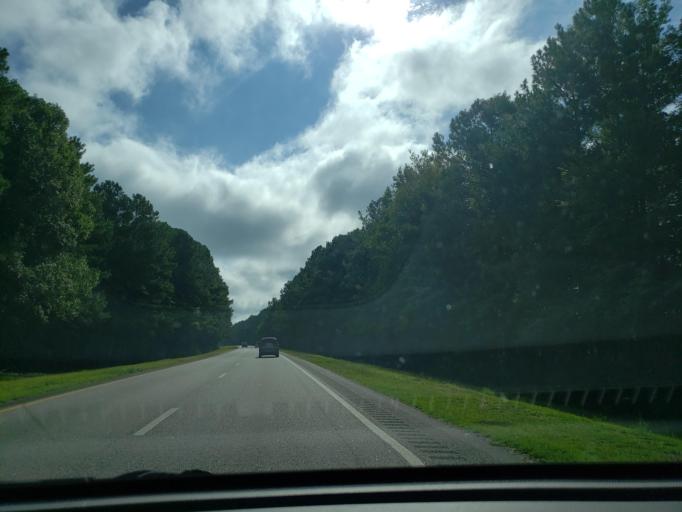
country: US
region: North Carolina
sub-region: Nash County
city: Spring Hope
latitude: 35.9305
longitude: -78.0854
